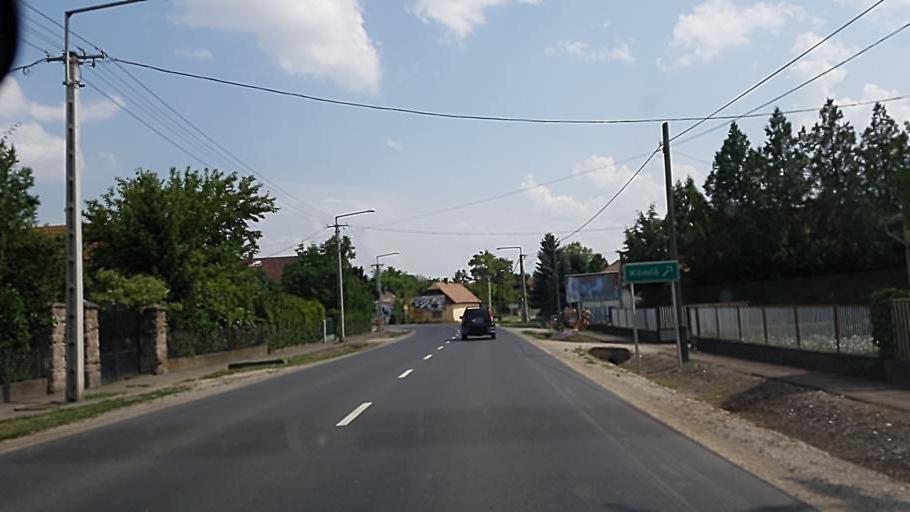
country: HU
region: Heves
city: Besenyotelek
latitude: 47.6961
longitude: 20.4325
